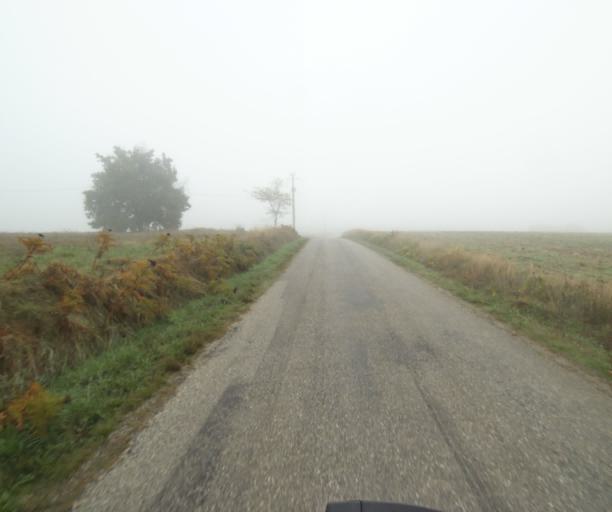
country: FR
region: Midi-Pyrenees
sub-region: Departement de la Haute-Garonne
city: Villemur-sur-Tarn
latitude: 43.9020
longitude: 1.4852
